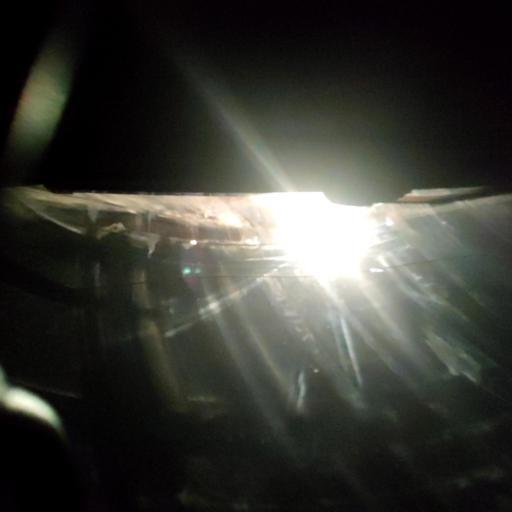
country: RU
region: Bashkortostan
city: Ulukulevo
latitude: 54.3710
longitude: 56.4207
